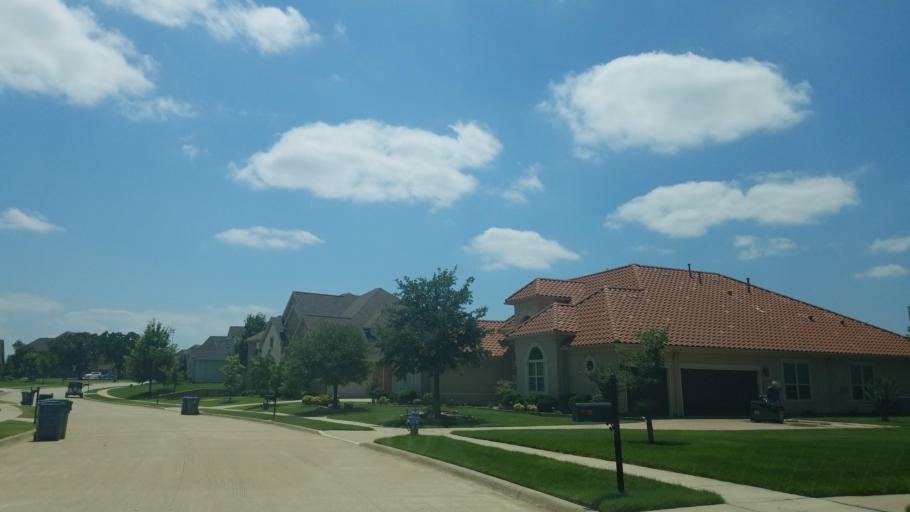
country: US
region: Texas
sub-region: Denton County
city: Copper Canyon
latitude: 33.0766
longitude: -97.0896
